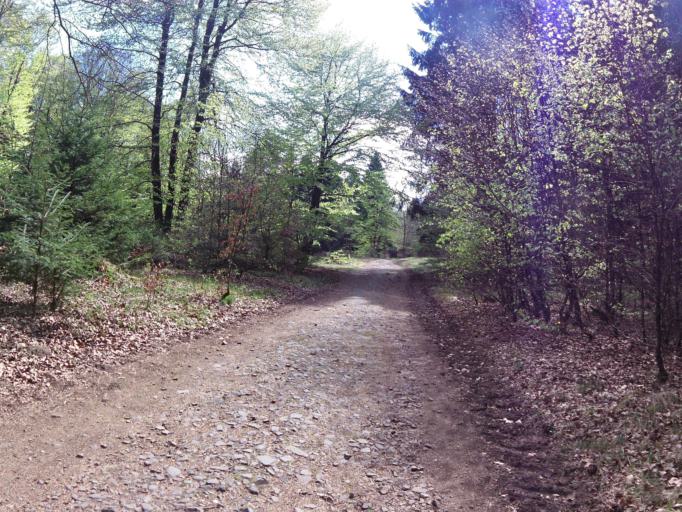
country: DE
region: Thuringia
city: Friedrichroda
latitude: 50.8229
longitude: 10.5401
